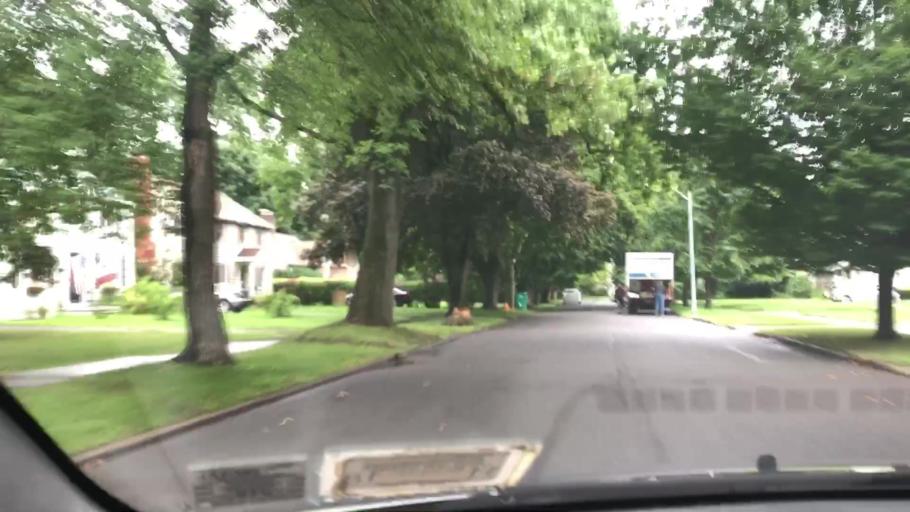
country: US
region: New York
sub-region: Monroe County
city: Brighton
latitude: 43.1253
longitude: -77.5588
